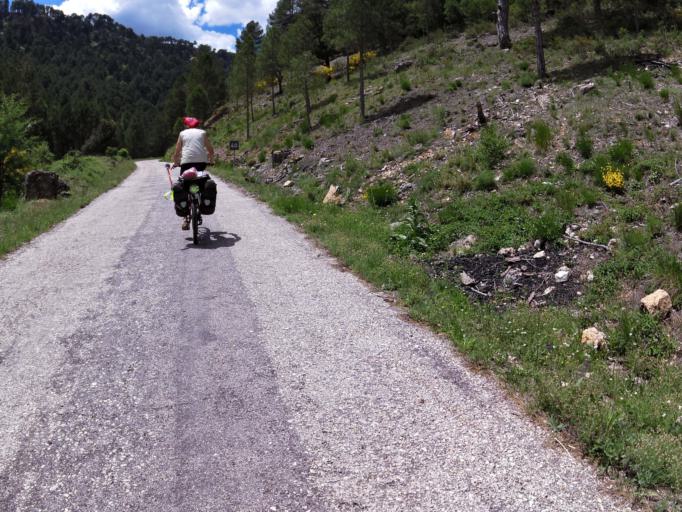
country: ES
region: Castille-La Mancha
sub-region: Provincia de Albacete
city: Paterna del Madera
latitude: 38.5721
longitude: -2.3571
